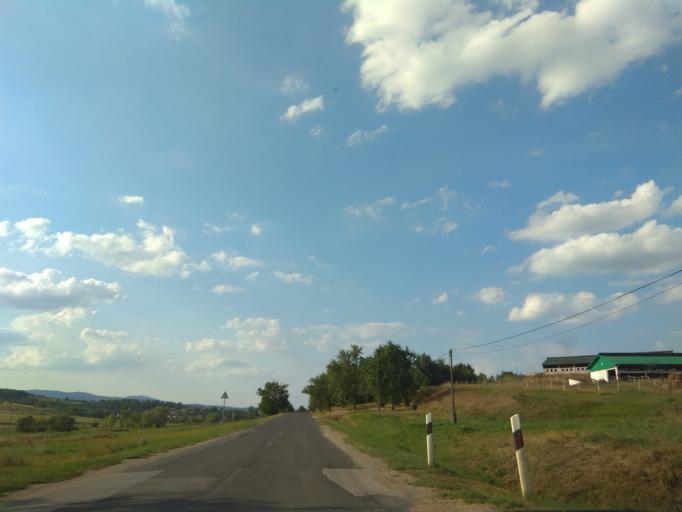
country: HU
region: Borsod-Abauj-Zemplen
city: Harsany
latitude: 47.9534
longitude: 20.7451
